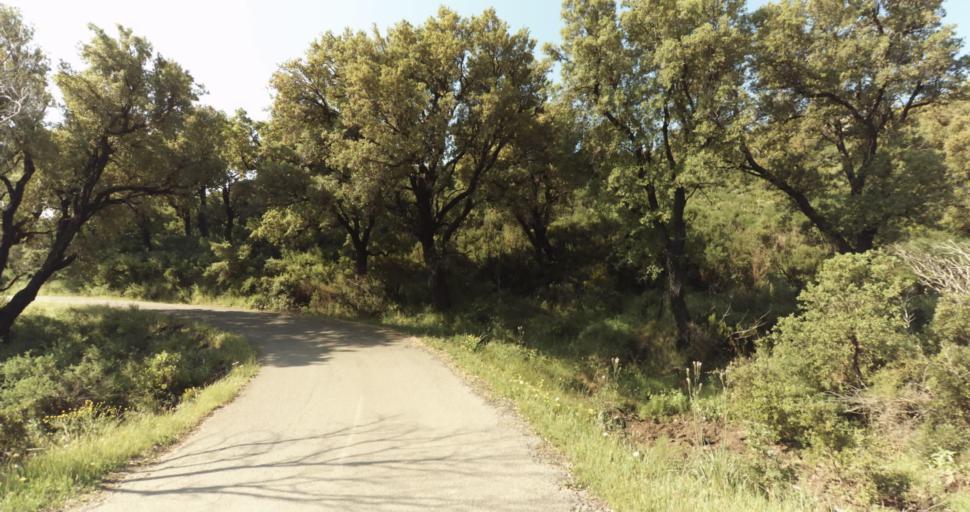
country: FR
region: Corsica
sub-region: Departement de la Haute-Corse
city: Biguglia
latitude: 42.6363
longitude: 9.4163
